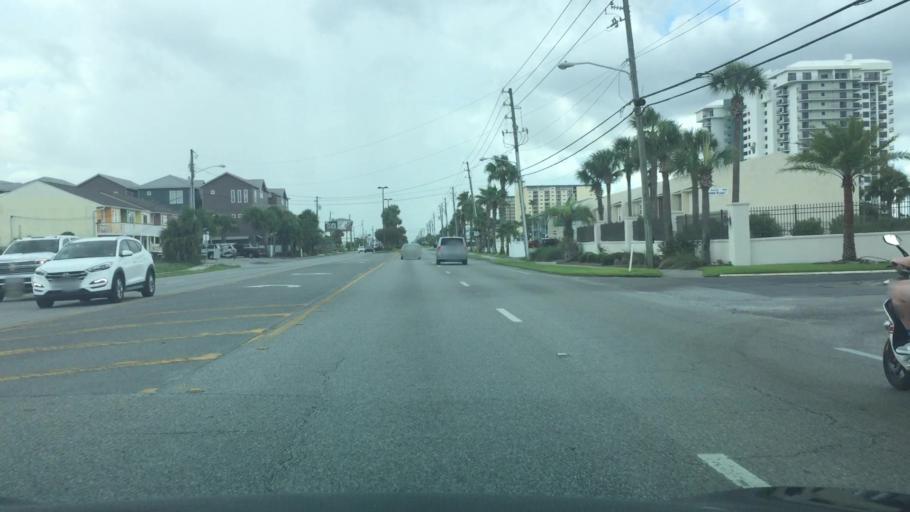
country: US
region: Florida
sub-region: Bay County
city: Lower Grand Lagoon
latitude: 30.1517
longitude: -85.7659
